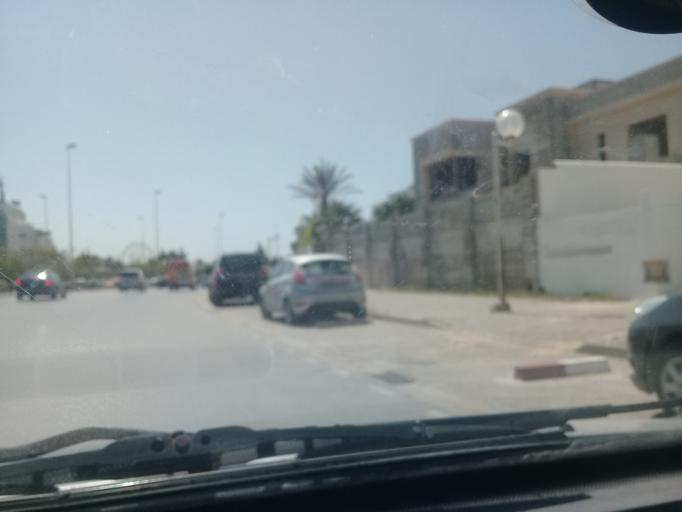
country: TN
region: Ariana
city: Ariana
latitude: 36.8336
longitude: 10.2332
